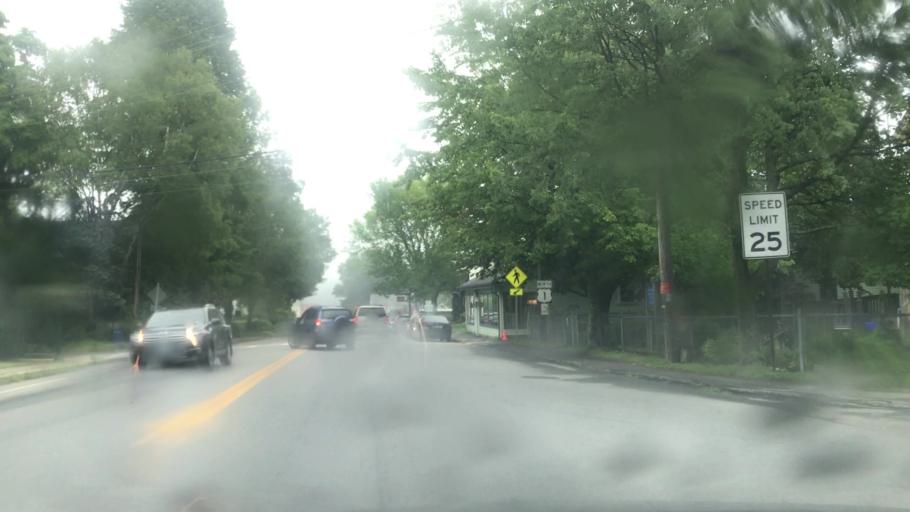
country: US
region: Maine
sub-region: Knox County
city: Camden
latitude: 44.2077
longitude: -69.0676
